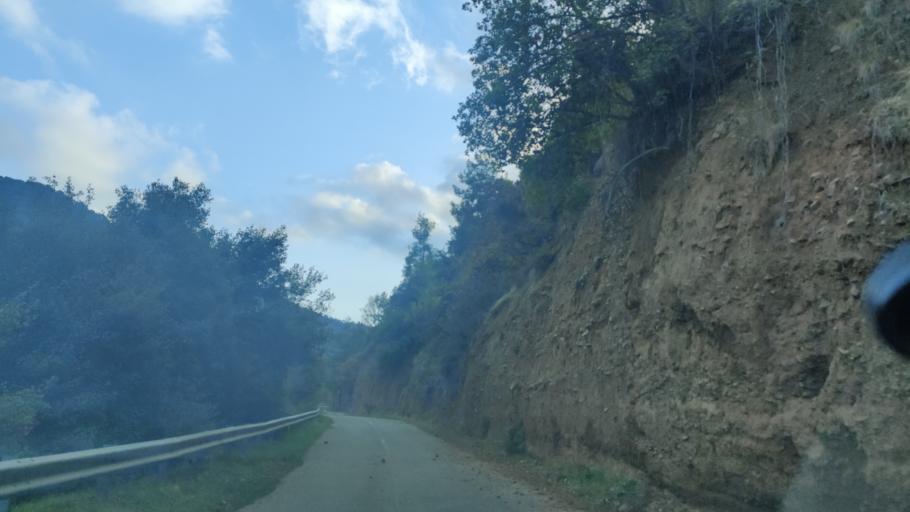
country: CY
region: Lefkosia
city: Lefka
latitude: 35.0535
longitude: 32.7349
